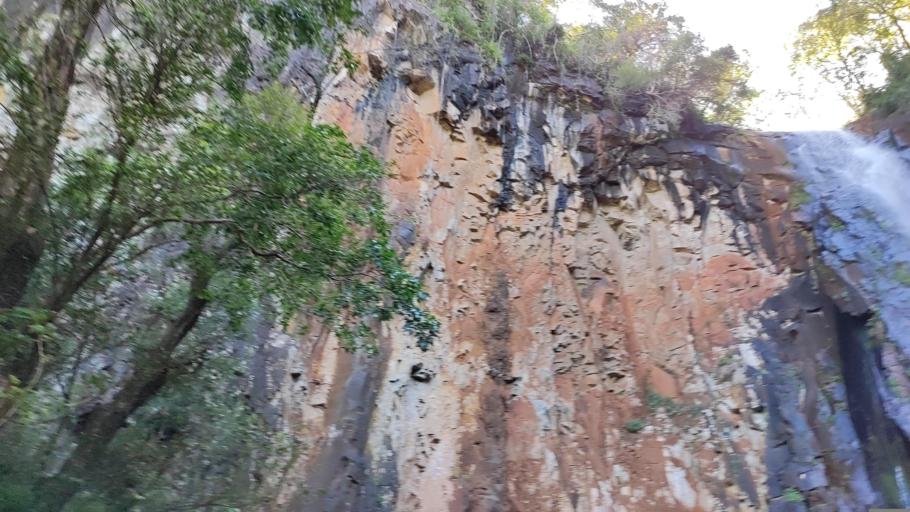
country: AR
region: Misiones
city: Dos de Mayo
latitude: -26.9930
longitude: -54.6310
